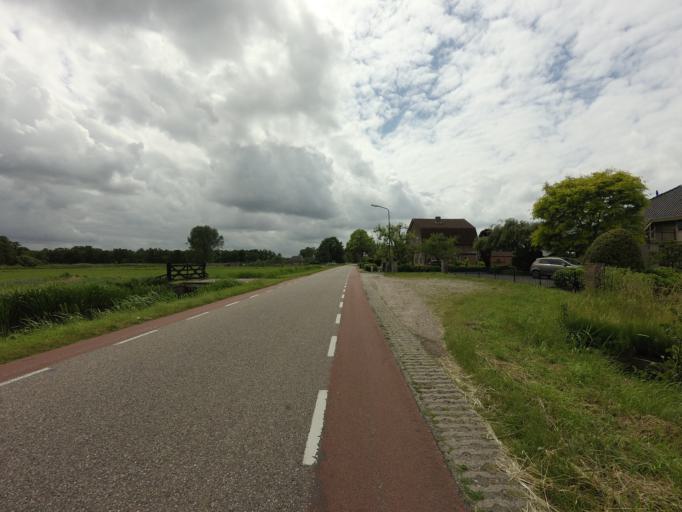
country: NL
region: North Holland
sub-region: Gemeente Wijdemeren
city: Kortenhoef
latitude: 52.2362
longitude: 5.1043
